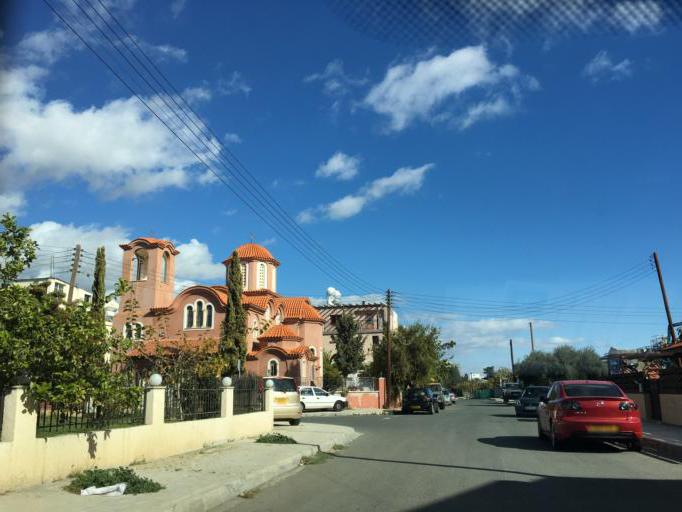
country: CY
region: Limassol
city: Limassol
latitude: 34.6588
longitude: 33.0116
